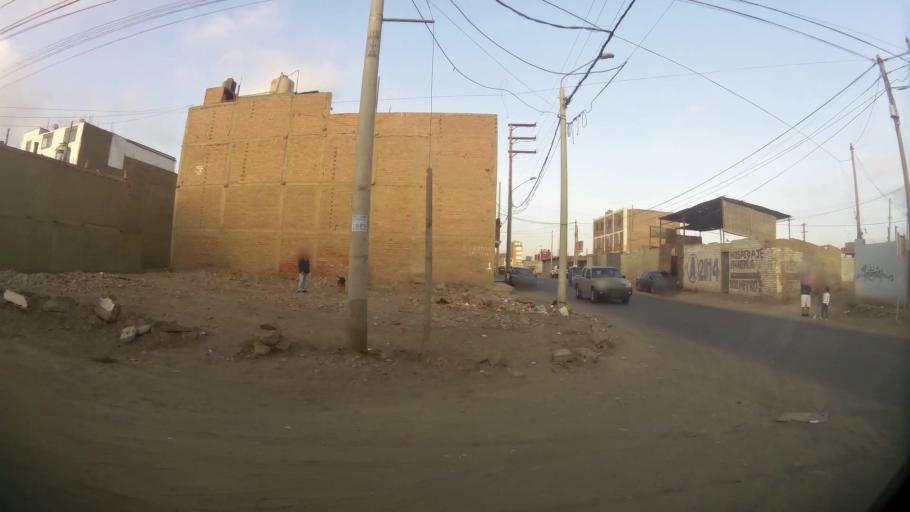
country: PE
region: Lima
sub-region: Huaura
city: Huacho
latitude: -11.1093
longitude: -77.5980
